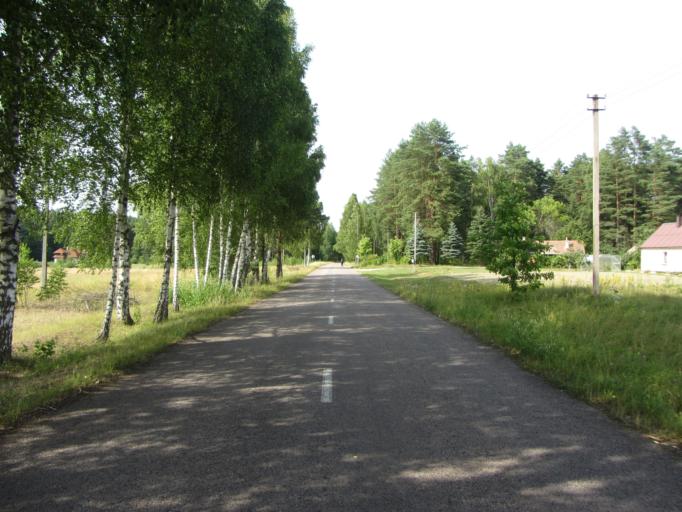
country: LT
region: Alytaus apskritis
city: Druskininkai
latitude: 54.0105
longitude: 23.9296
